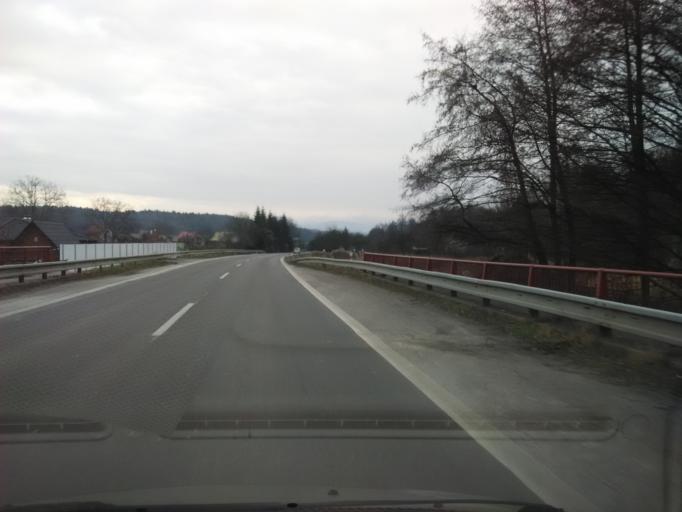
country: SK
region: Nitriansky
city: Prievidza
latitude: 48.8528
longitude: 18.6440
